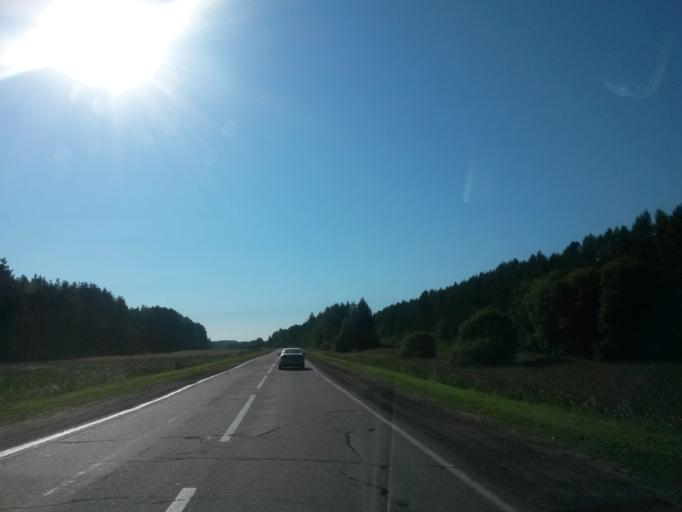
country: RU
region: Jaroslavl
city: Krasnyye Tkachi
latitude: 57.3924
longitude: 39.6814
